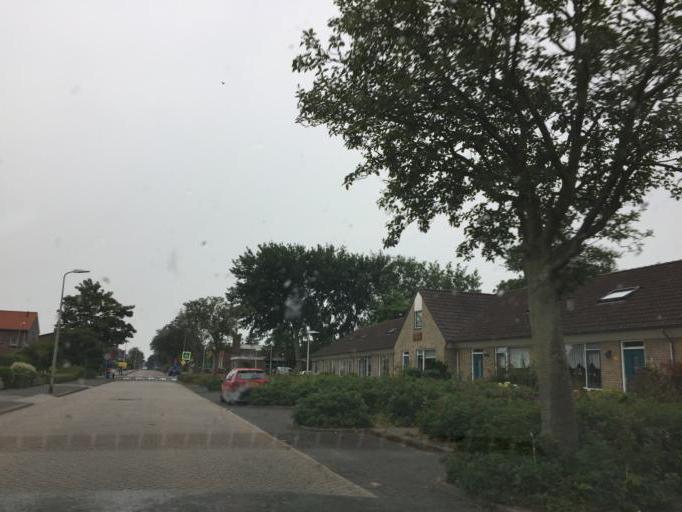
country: NL
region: North Holland
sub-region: Gemeente Texel
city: Den Burg
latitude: 53.0554
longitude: 4.7915
